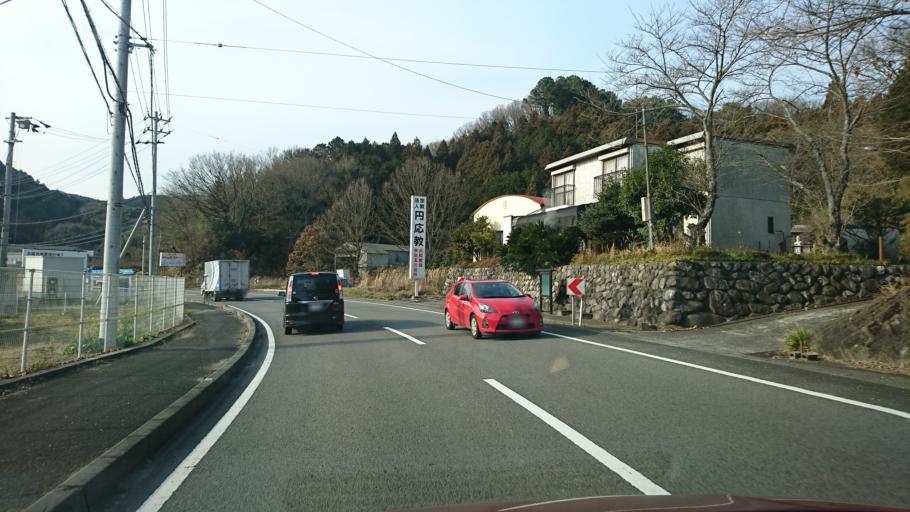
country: JP
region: Ehime
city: Hojo
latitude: 33.9964
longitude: 132.9243
